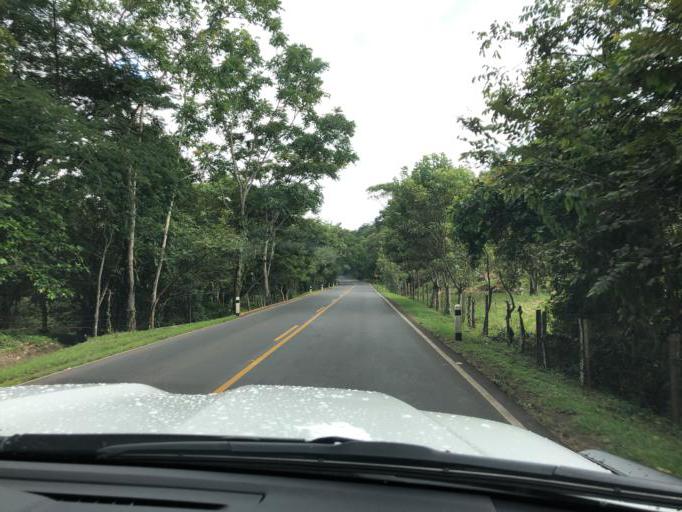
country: NI
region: Chontales
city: Villa Sandino
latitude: 11.9980
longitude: -84.8860
